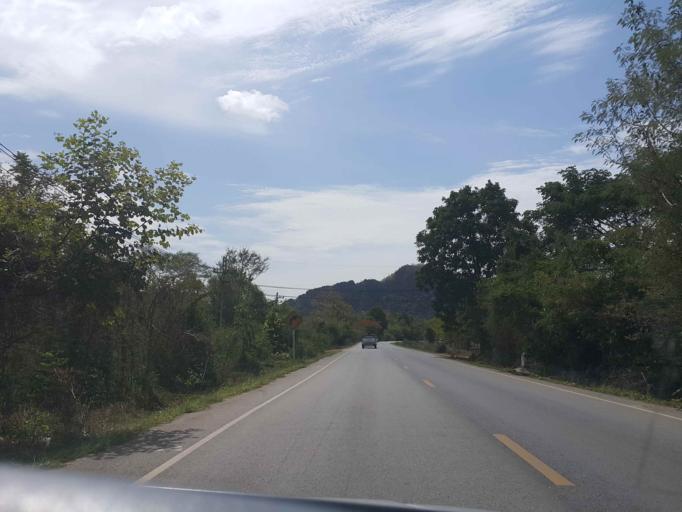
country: TH
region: Sukhothai
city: Thung Saliam
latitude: 17.3349
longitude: 99.4897
